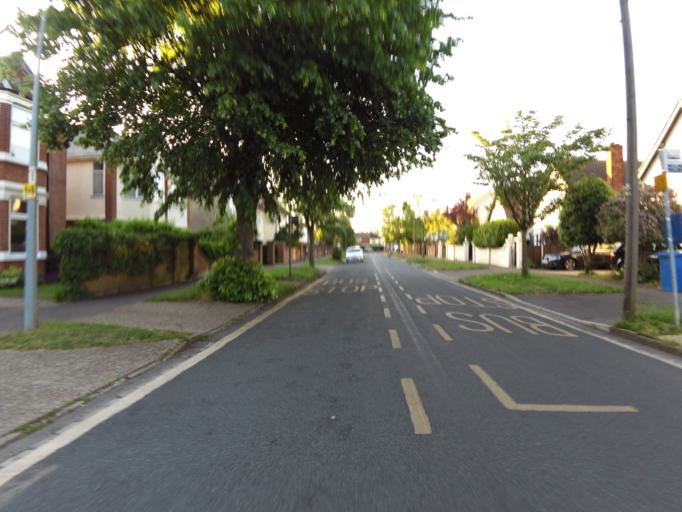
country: GB
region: England
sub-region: Suffolk
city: Ipswich
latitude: 52.0594
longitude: 1.1947
